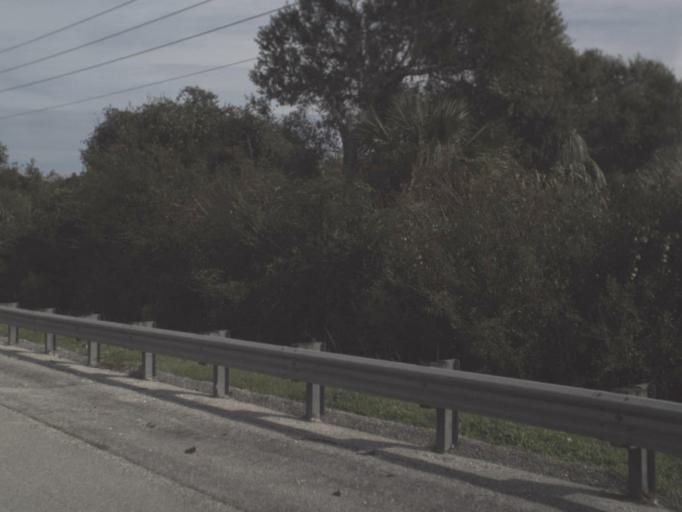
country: US
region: Florida
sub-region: DeSoto County
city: Nocatee
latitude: 27.0530
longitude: -81.7849
